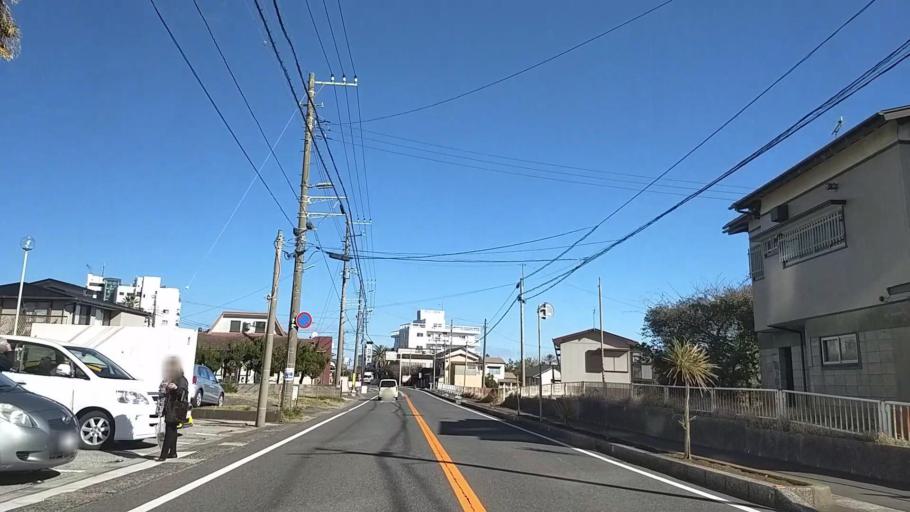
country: JP
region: Chiba
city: Tateyama
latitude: 34.9772
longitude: 139.9650
